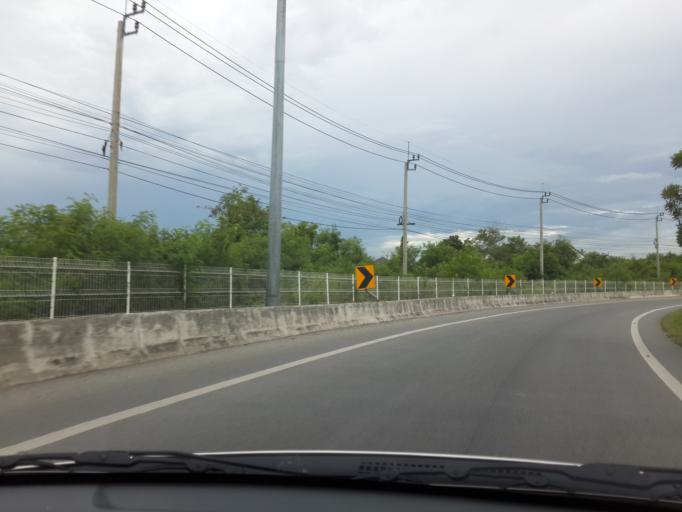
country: TH
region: Bangkok
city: Saphan Sung
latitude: 13.7813
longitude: 100.6889
